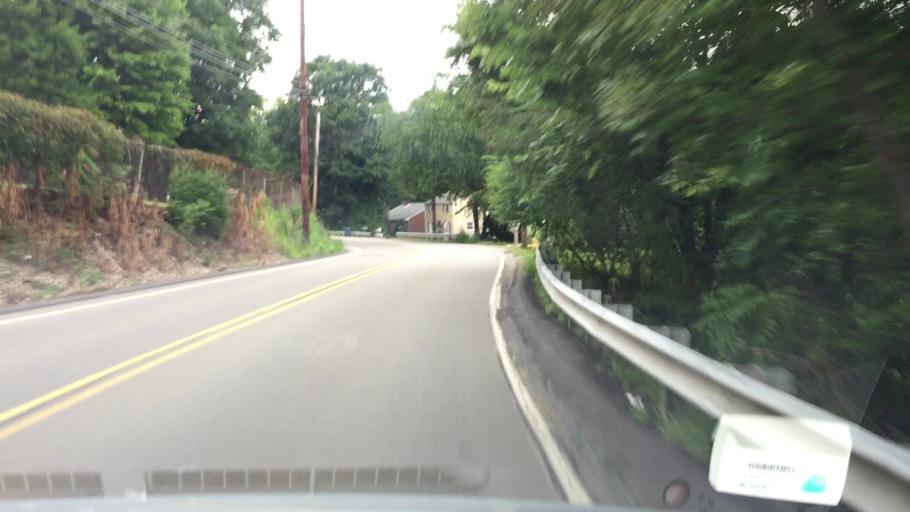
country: US
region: Pennsylvania
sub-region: Allegheny County
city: Glenshaw
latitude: 40.5185
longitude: -79.9828
